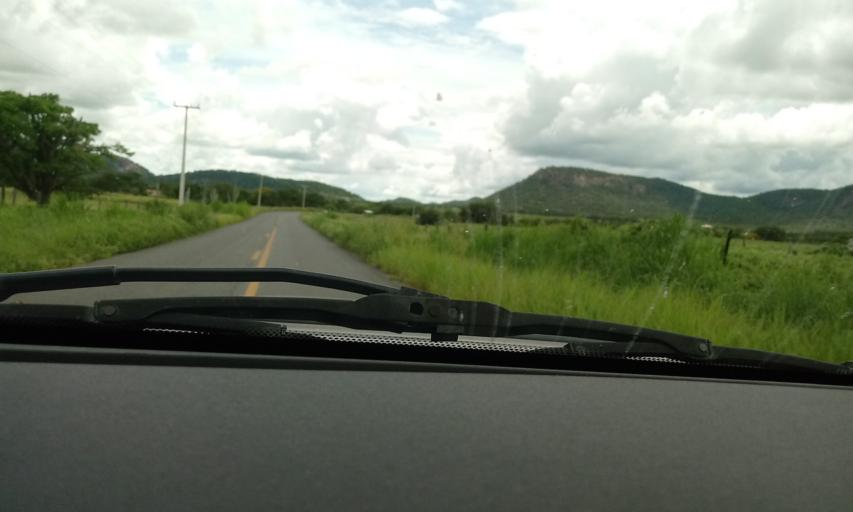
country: BR
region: Bahia
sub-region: Guanambi
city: Guanambi
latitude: -14.1531
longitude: -42.8239
